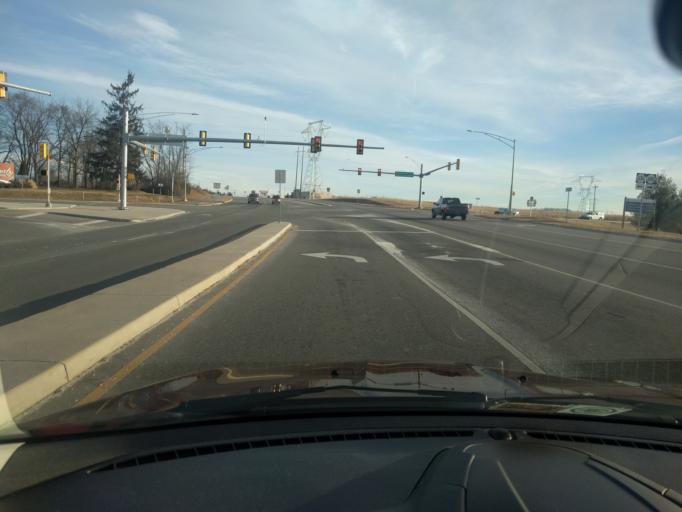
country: US
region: Virginia
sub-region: Augusta County
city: Fishersville
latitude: 38.0869
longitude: -78.9822
